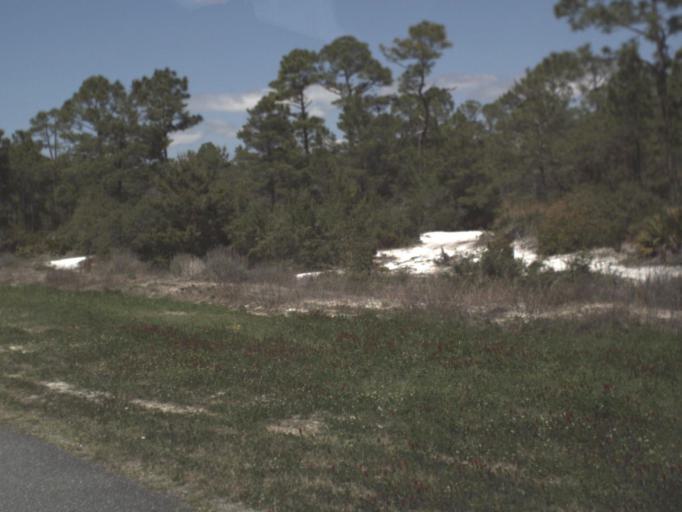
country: US
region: Florida
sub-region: Bay County
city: Mexico Beach
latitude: 29.8895
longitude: -85.3553
